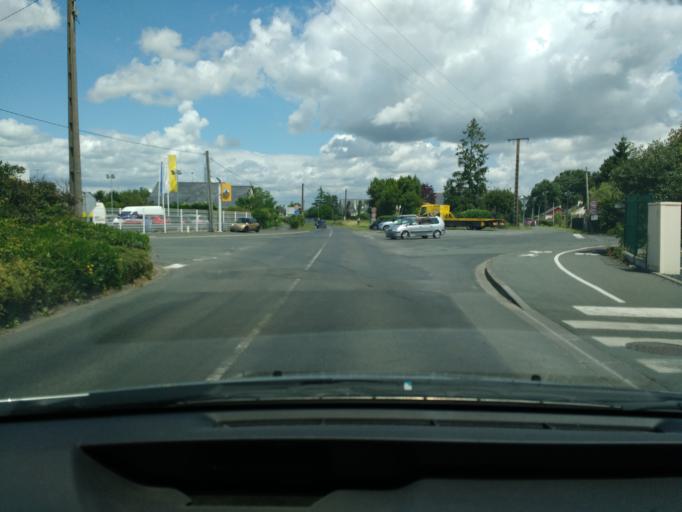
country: FR
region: Pays de la Loire
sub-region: Departement de Maine-et-Loire
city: Trelaze
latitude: 47.4737
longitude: -0.4927
